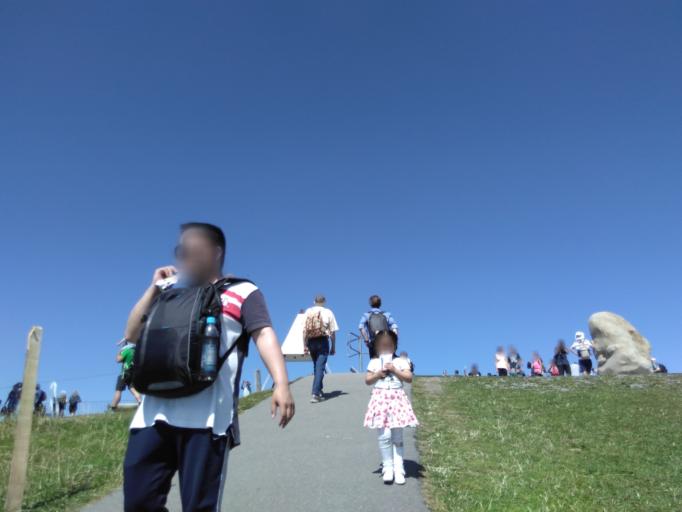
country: CH
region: Schwyz
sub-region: Bezirk Schwyz
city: Arth
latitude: 47.0565
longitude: 8.4854
